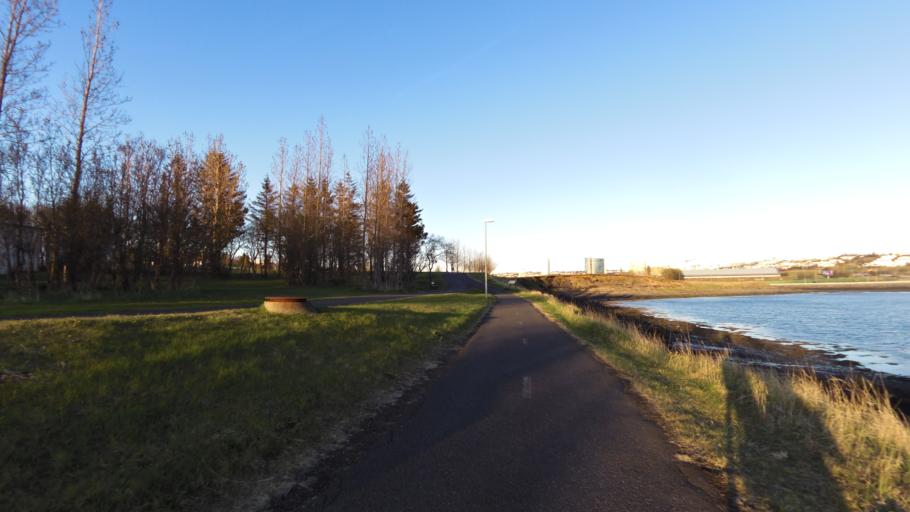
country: IS
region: Capital Region
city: Kopavogur
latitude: 64.1058
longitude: -21.9109
